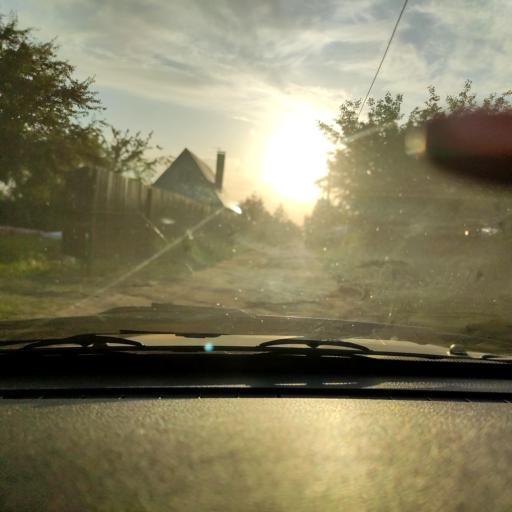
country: RU
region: Voronezj
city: Podgornoye
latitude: 51.8343
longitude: 39.1930
